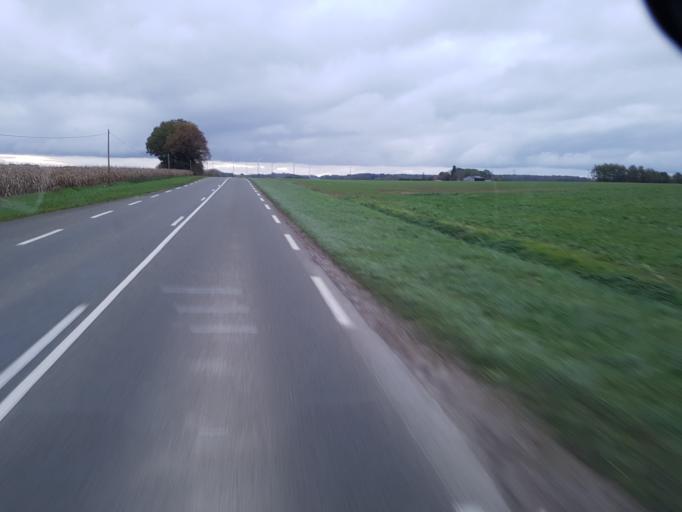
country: FR
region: Champagne-Ardenne
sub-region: Departement de la Marne
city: Montmirail
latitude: 48.8879
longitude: 3.5016
